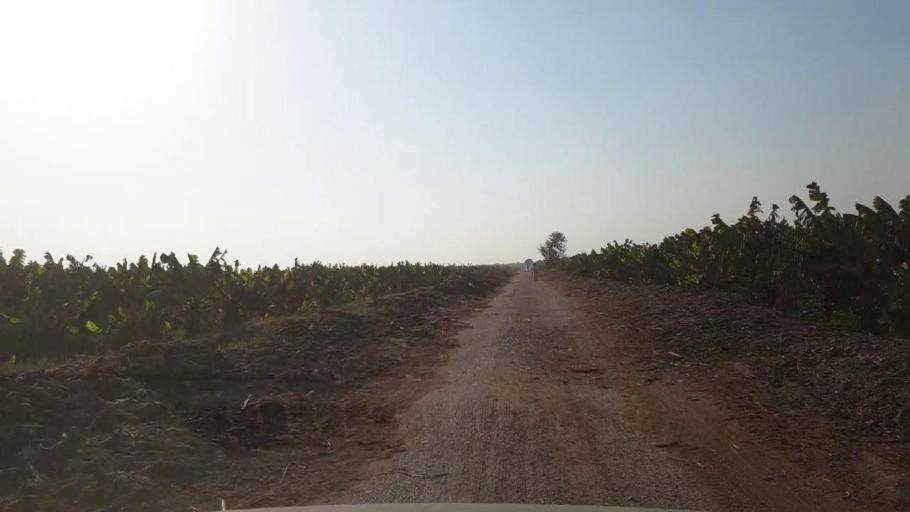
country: PK
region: Sindh
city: Tando Allahyar
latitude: 25.3467
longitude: 68.6711
